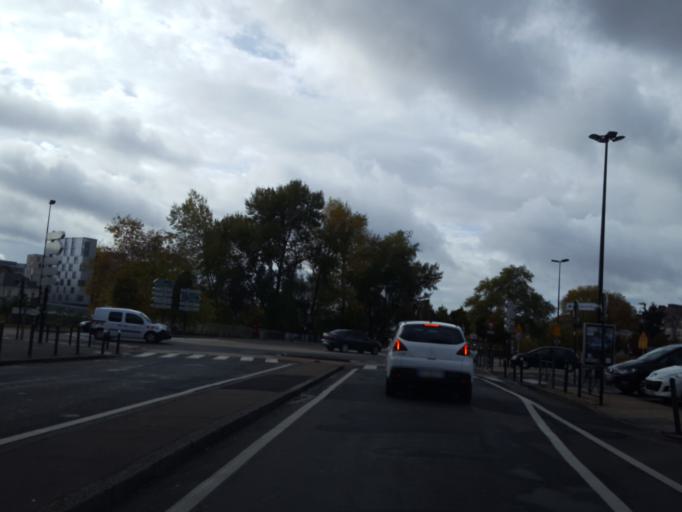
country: FR
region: Pays de la Loire
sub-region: Departement de la Loire-Atlantique
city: Nantes
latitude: 47.2103
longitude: -1.5609
